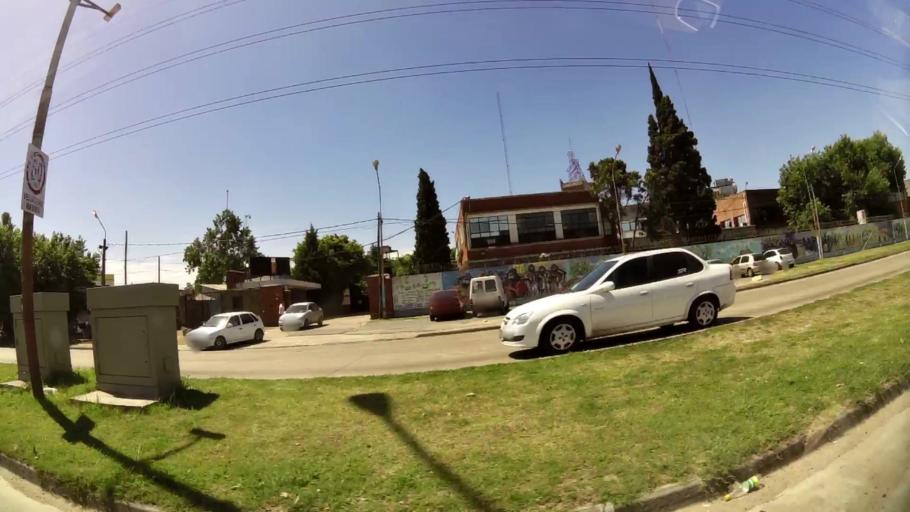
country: AR
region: Buenos Aires
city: Caseros
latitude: -34.5645
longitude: -58.5719
